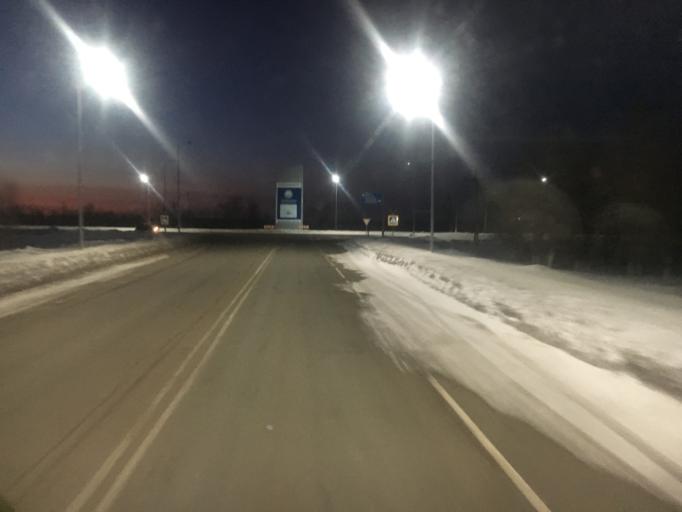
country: KZ
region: Batys Qazaqstan
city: Oral
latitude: 51.1648
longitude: 51.5246
